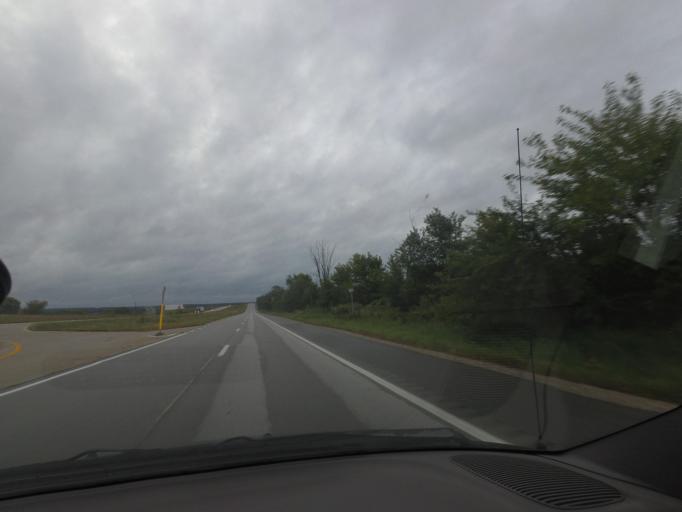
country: US
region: Missouri
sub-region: Shelby County
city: Shelbina
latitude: 39.6695
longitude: -91.9370
